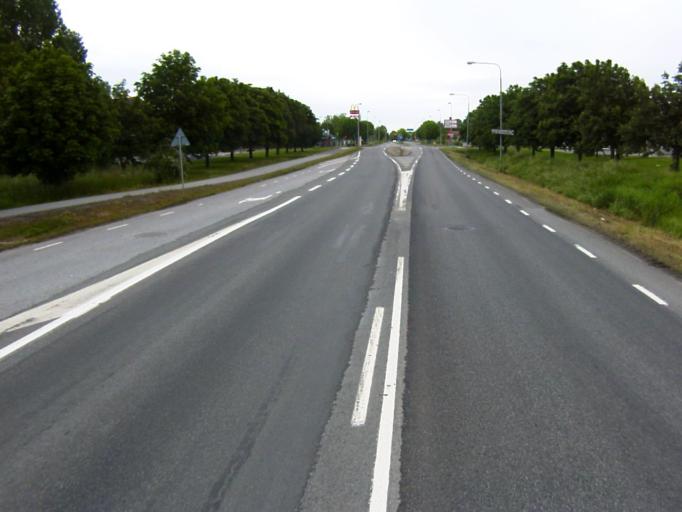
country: SE
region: Skane
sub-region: Kristianstads Kommun
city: Kristianstad
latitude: 56.0247
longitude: 14.1417
